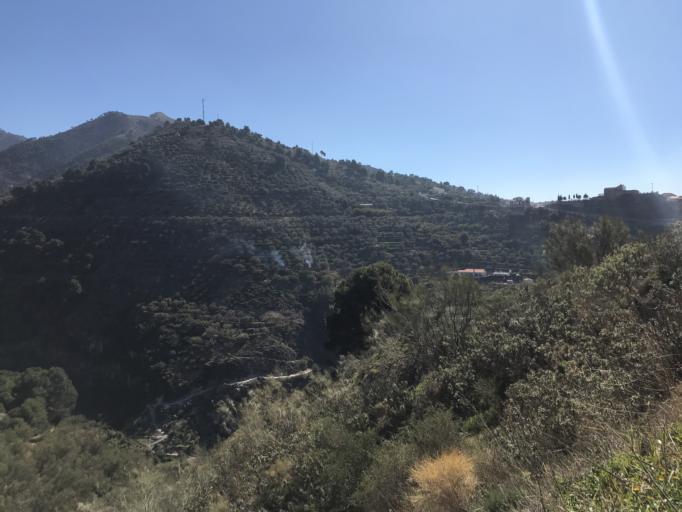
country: ES
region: Andalusia
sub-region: Provincia de Malaga
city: Canillas de Albaida
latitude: 36.8521
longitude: -3.9877
